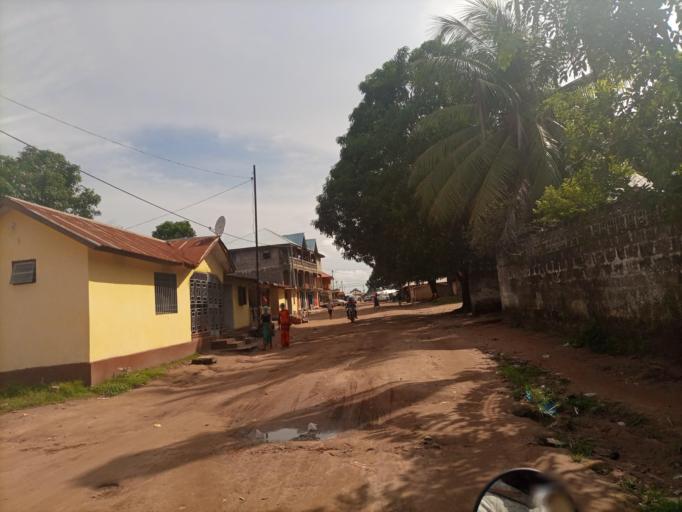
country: SL
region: Northern Province
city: Masoyila
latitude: 8.6047
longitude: -13.1782
